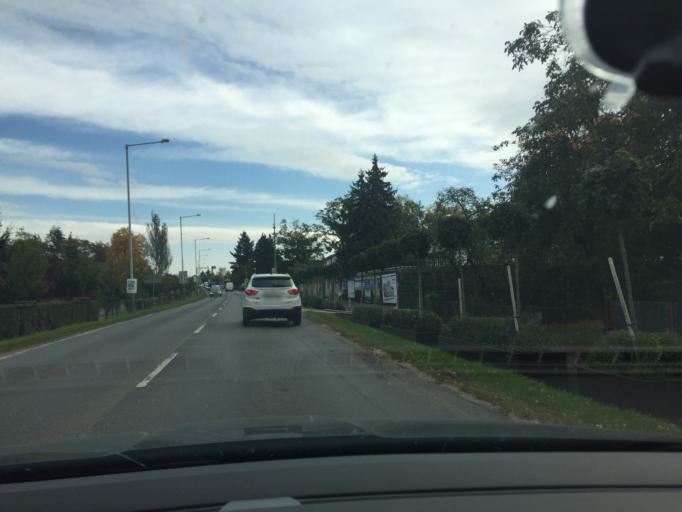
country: CZ
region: Praha
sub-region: Praha 20
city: Horni Pocernice
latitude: 50.0807
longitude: 14.6191
